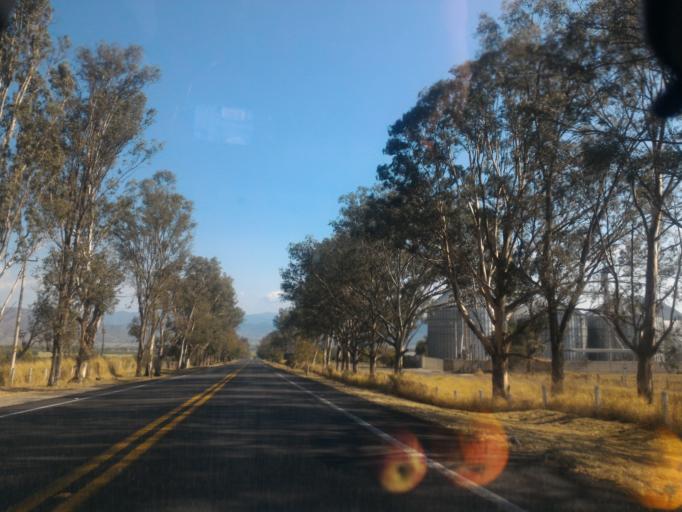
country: MX
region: Jalisco
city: Tuxpan
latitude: 19.5476
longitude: -103.4317
